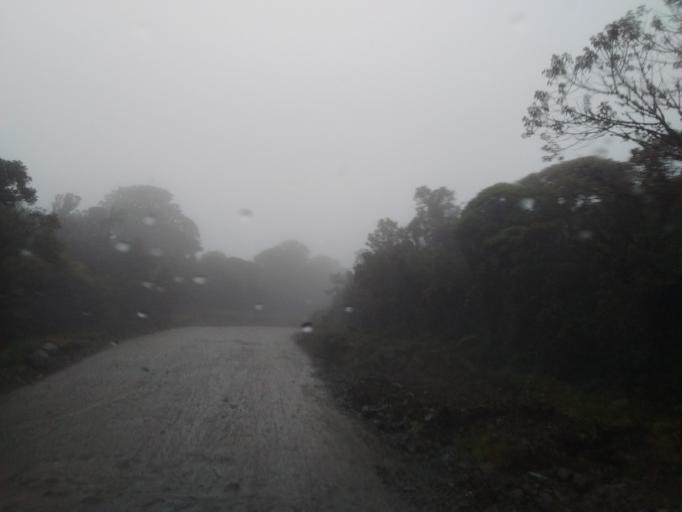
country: CO
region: Cauca
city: Paispamba
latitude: 2.1531
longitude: -76.4191
